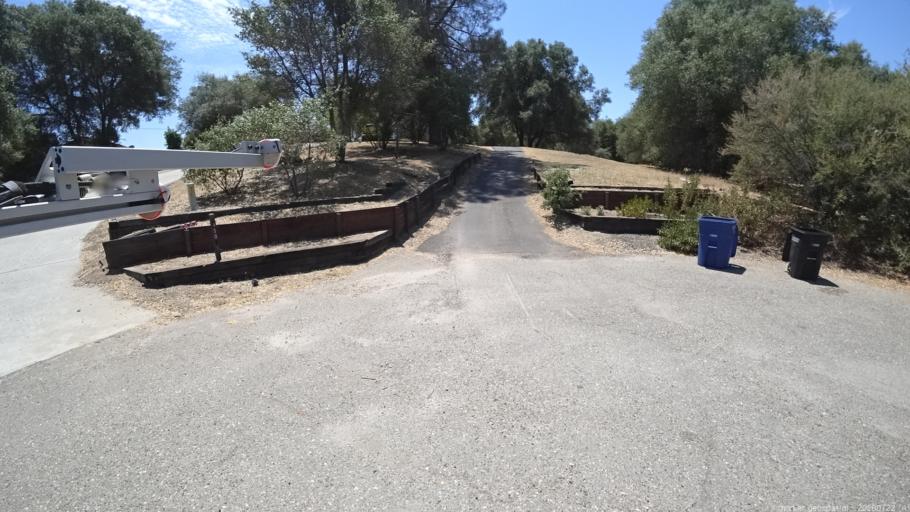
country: US
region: California
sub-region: Madera County
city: Coarsegold
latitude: 37.2474
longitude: -119.7267
